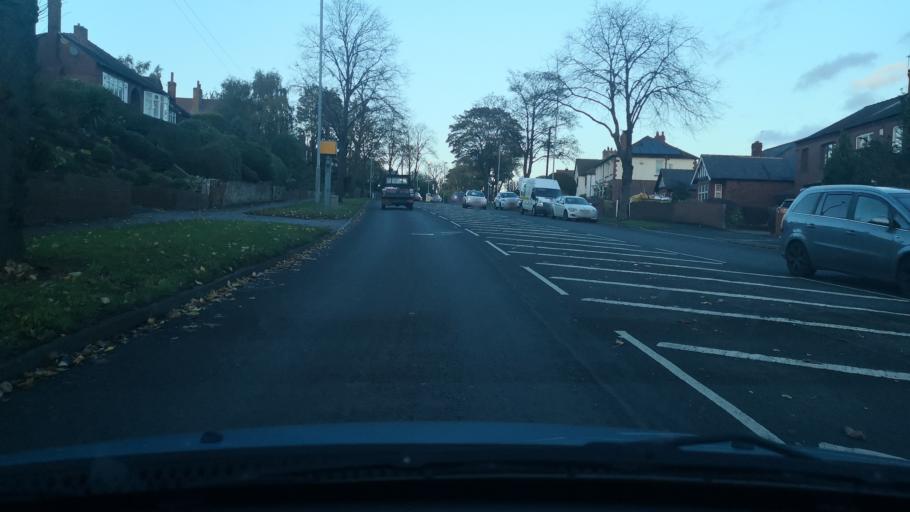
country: GB
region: England
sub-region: City and Borough of Wakefield
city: Horbury
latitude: 53.6662
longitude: -1.5383
